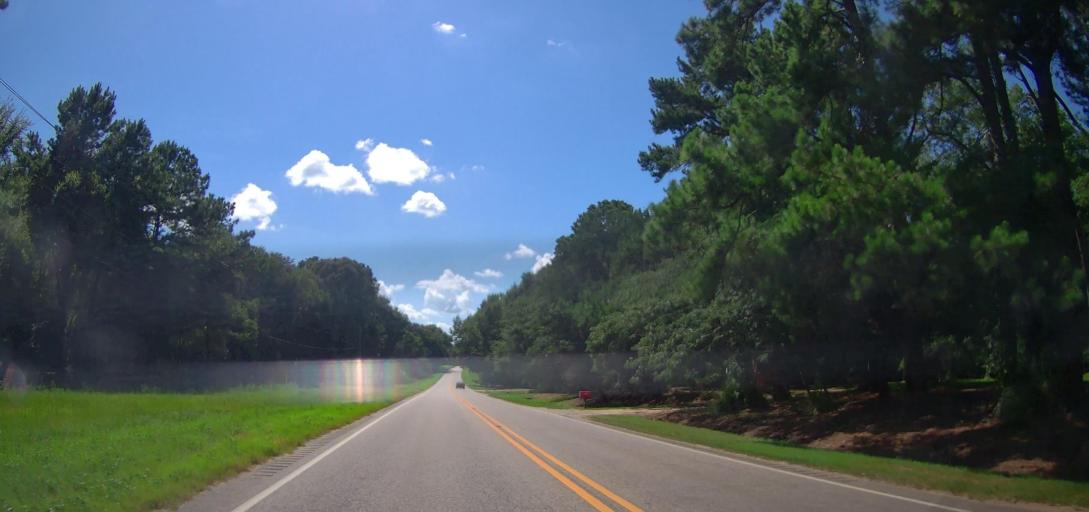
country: US
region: Alabama
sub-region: Elmore County
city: Tallassee
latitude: 32.3788
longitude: -85.8645
